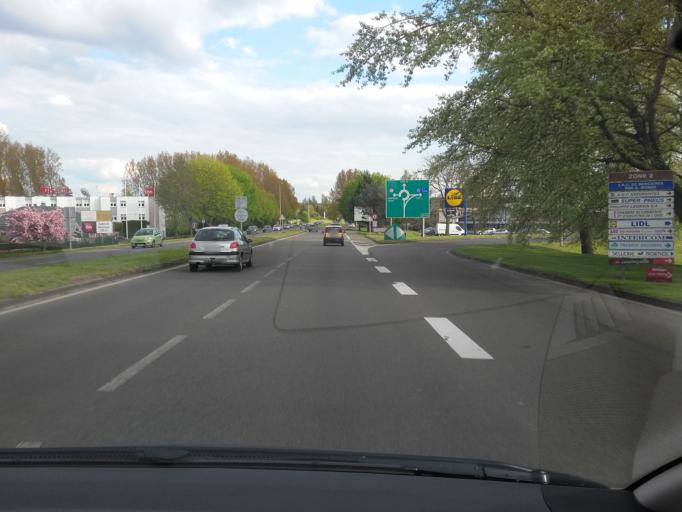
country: FR
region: Picardie
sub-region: Departement de l'Oise
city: Jaux
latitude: 49.3974
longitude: 2.7882
